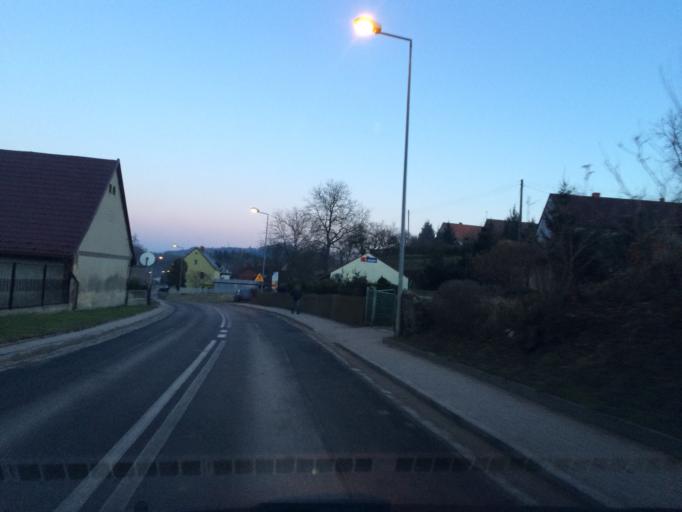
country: PL
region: Lower Silesian Voivodeship
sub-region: Powiat zlotoryjski
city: Zlotoryja
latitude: 51.1148
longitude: 15.8768
